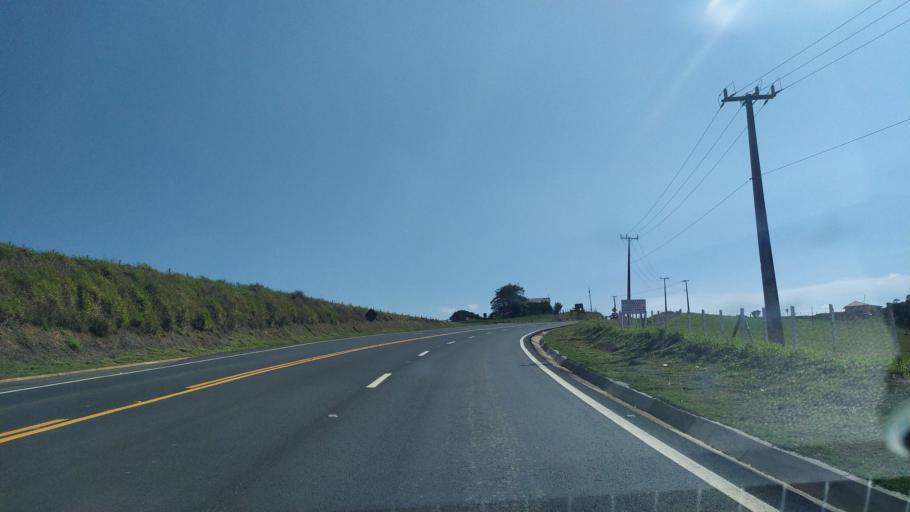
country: BR
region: Parana
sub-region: Telemaco Borba
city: Telemaco Borba
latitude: -24.2841
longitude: -50.7117
